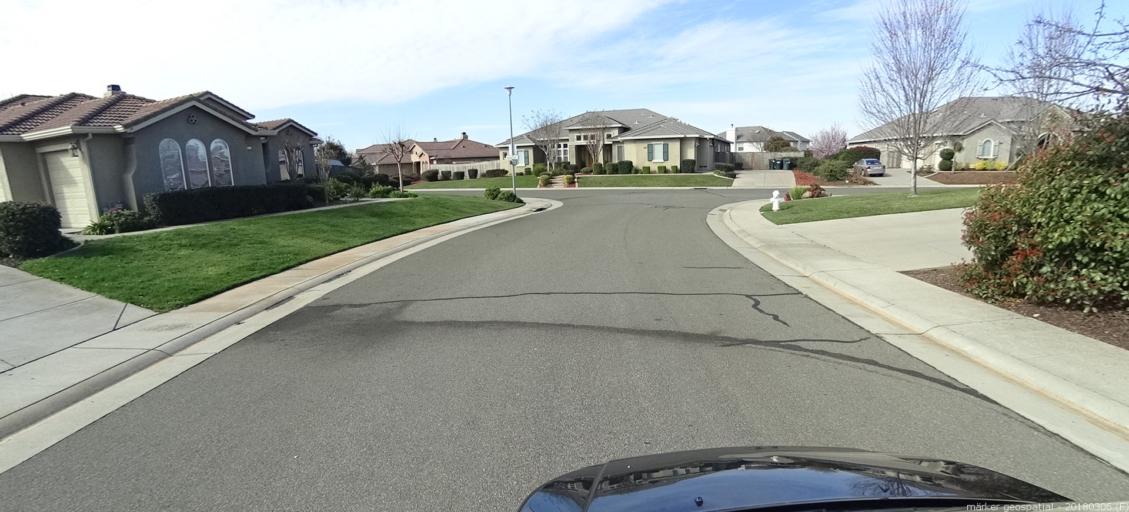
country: US
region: California
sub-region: Sacramento County
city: Vineyard
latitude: 38.4722
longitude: -121.3078
